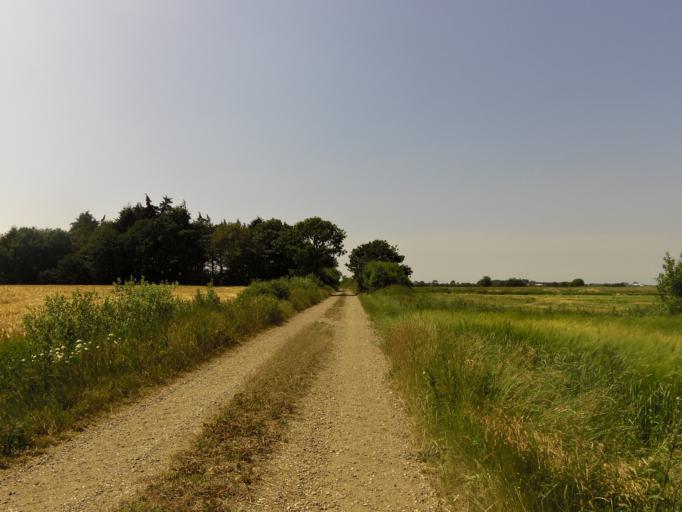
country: DK
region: South Denmark
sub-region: Aabenraa Kommune
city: Rodekro
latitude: 55.1430
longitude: 9.2344
